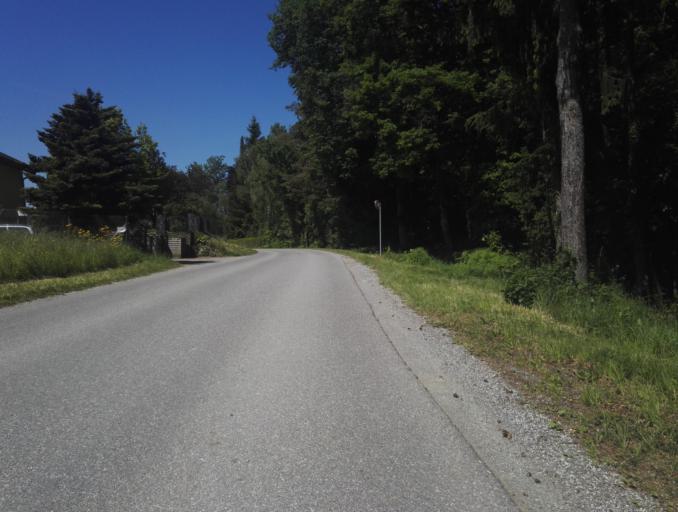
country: AT
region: Styria
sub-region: Politischer Bezirk Graz-Umgebung
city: Edelsgrub
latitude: 47.0541
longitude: 15.5776
